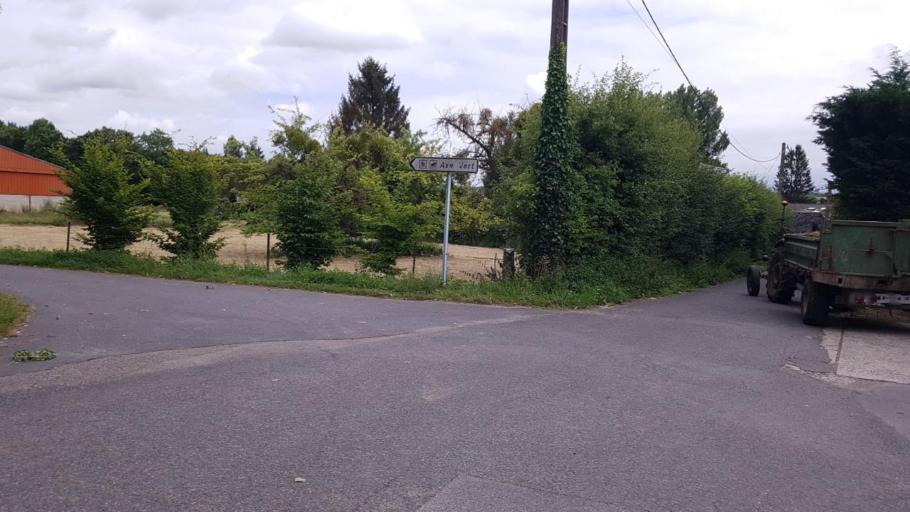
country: FR
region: Picardie
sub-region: Departement de l'Aisne
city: La Capelle
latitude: 49.9061
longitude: 3.9149
